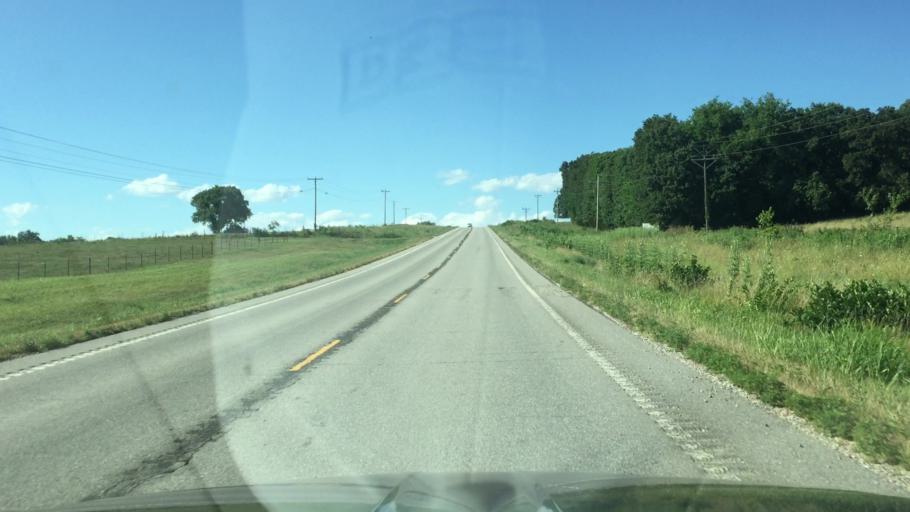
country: US
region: Missouri
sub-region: Moniteau County
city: Tipton
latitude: 38.5572
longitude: -92.7974
